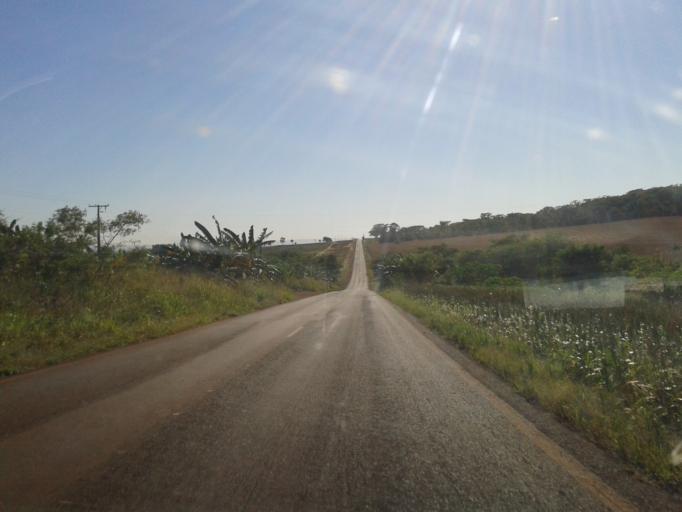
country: BR
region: Minas Gerais
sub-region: Capinopolis
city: Capinopolis
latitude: -18.6460
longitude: -49.5482
